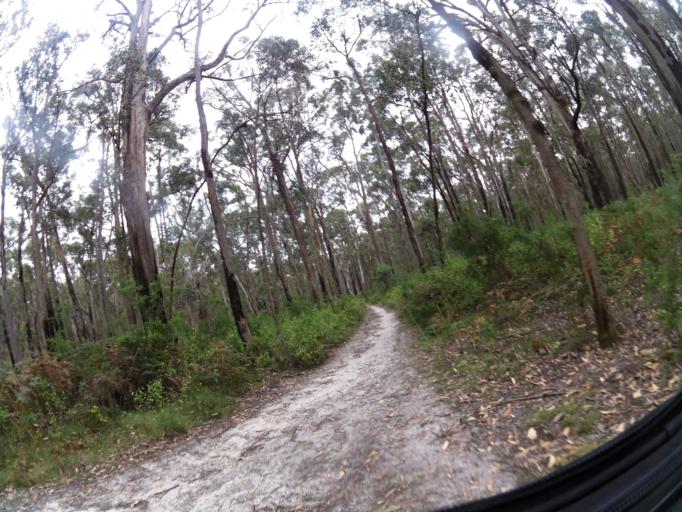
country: AU
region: Victoria
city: Brown Hill
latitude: -37.4931
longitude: 143.9082
